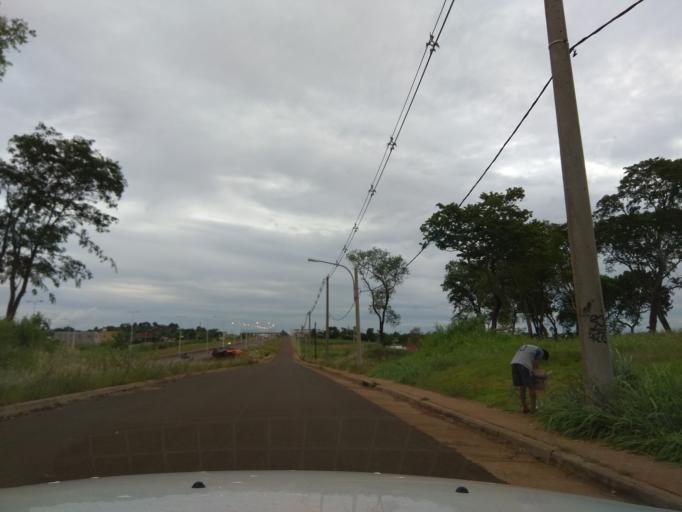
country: AR
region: Misiones
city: Garupa
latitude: -27.4451
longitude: -55.8493
